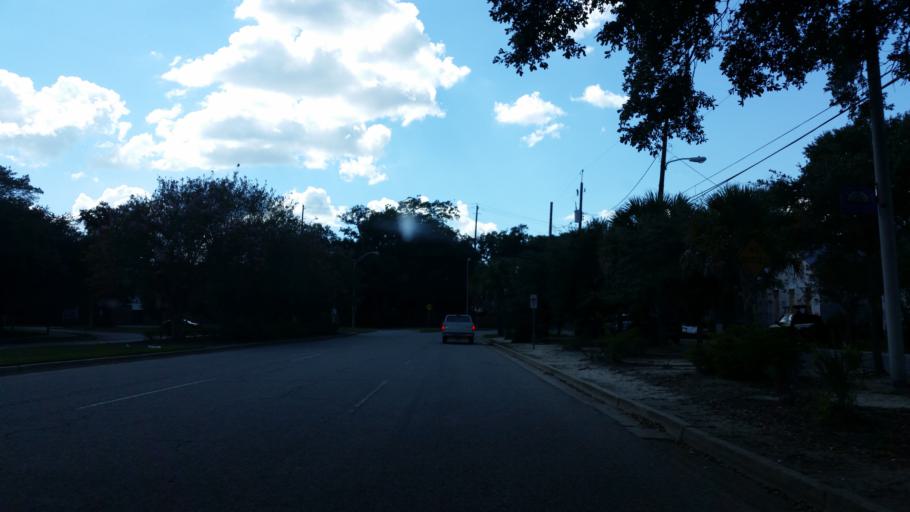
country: US
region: Alabama
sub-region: Mobile County
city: Mobile
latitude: 30.6844
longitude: -88.0518
